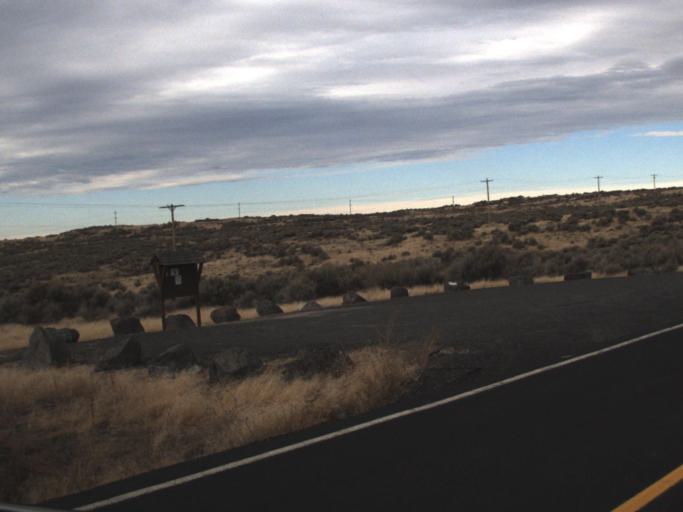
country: US
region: Washington
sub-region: Adams County
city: Ritzville
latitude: 47.4231
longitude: -118.6982
